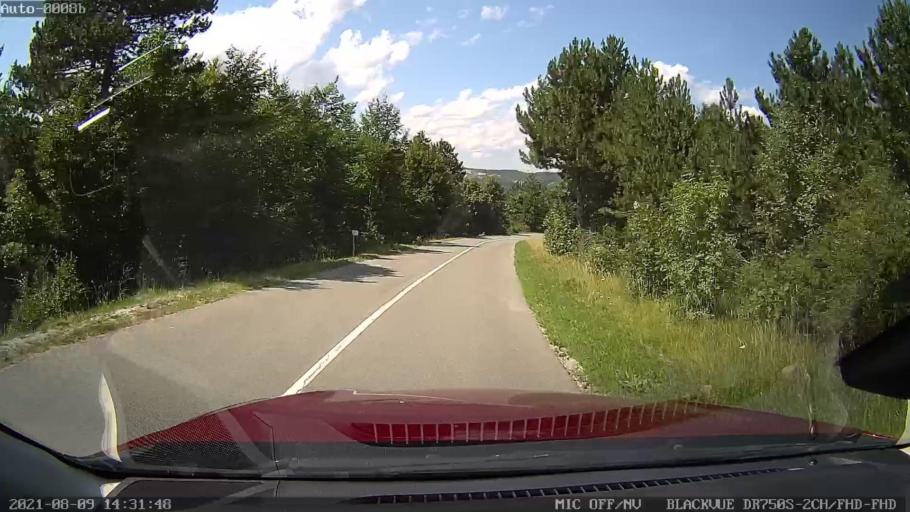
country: HR
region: Istarska
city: Lovran
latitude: 45.3076
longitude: 14.1933
